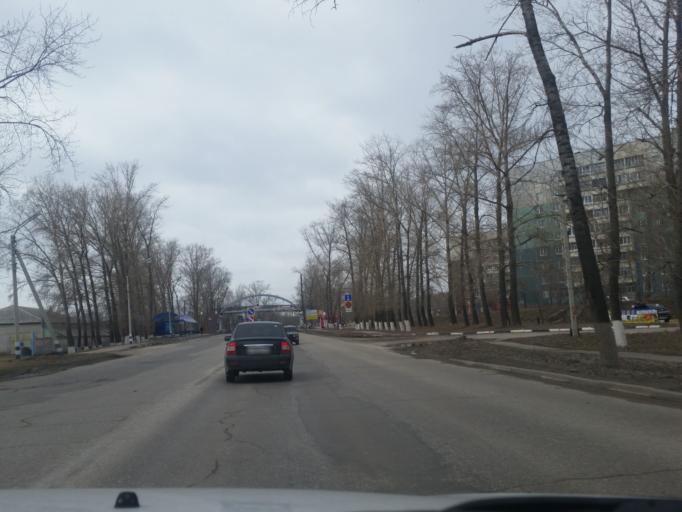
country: RU
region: Ulyanovsk
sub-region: Ulyanovskiy Rayon
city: Ulyanovsk
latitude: 54.3213
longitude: 48.4790
